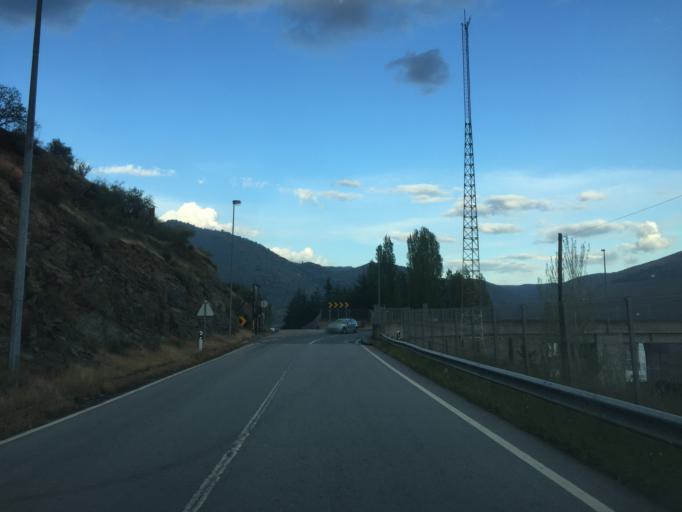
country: PT
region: Braganca
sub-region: Torre de Moncorvo
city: Torre de Moncorvo
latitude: 41.1364
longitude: -7.1154
